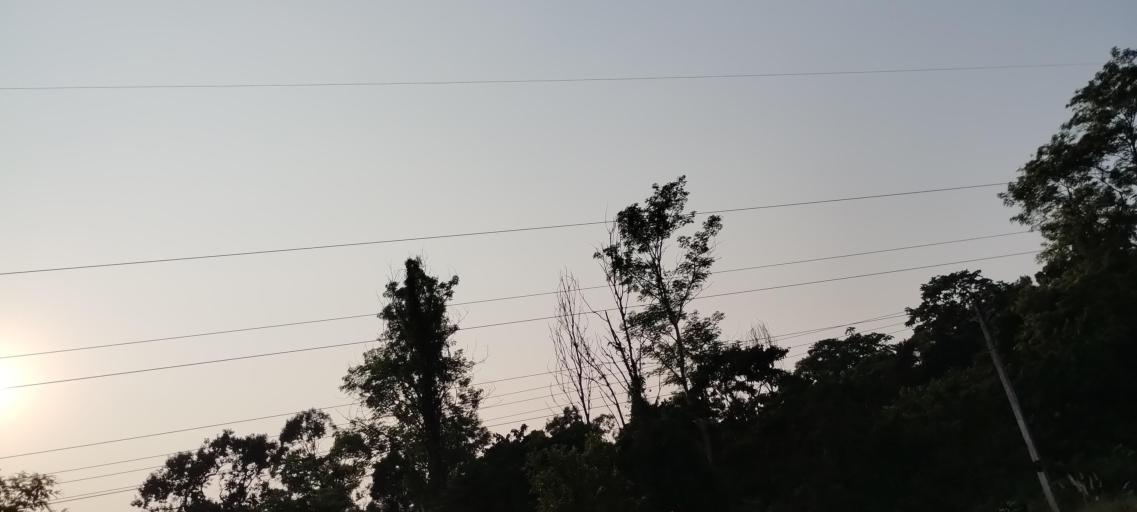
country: NP
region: Far Western
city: Tikapur
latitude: 28.5054
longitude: 81.3243
